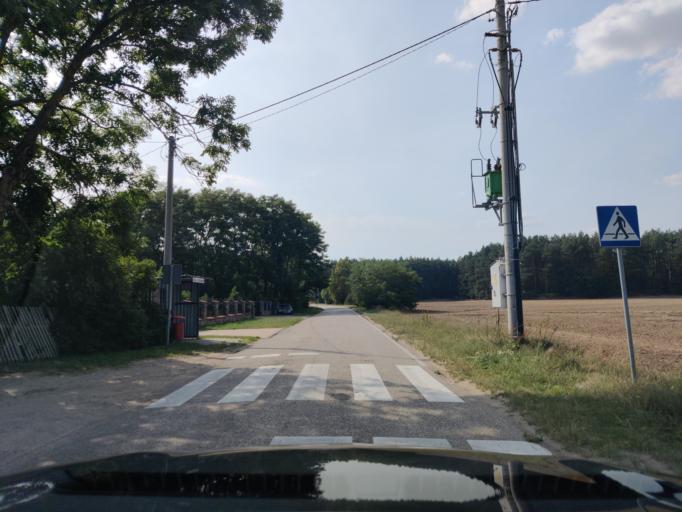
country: PL
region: Masovian Voivodeship
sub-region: Powiat wyszkowski
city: Rzasnik
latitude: 52.7659
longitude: 21.3905
